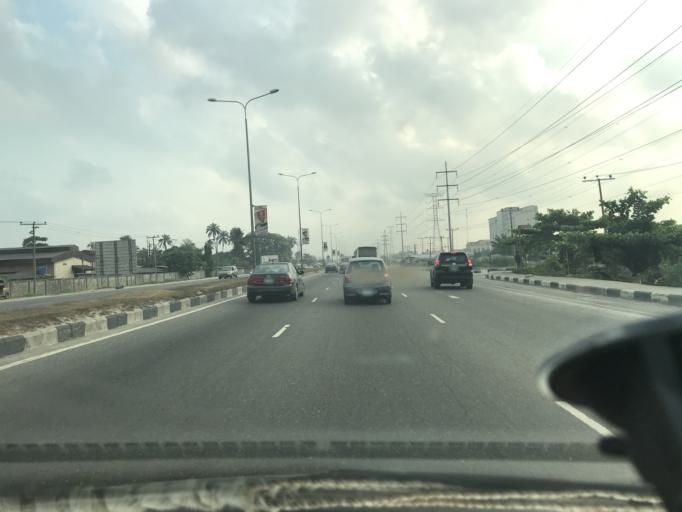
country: NG
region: Lagos
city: Ikoyi
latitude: 6.4468
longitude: 3.5444
